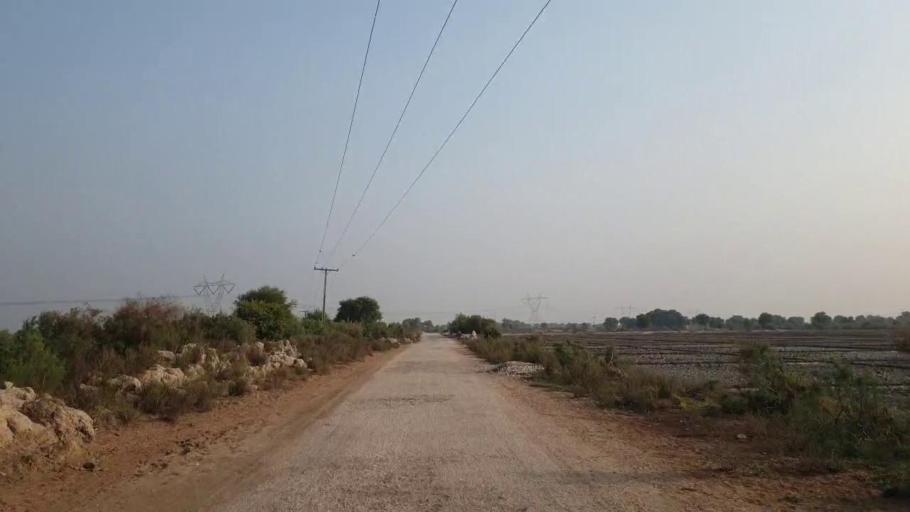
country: PK
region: Sindh
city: Bhan
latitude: 26.4954
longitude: 67.7692
